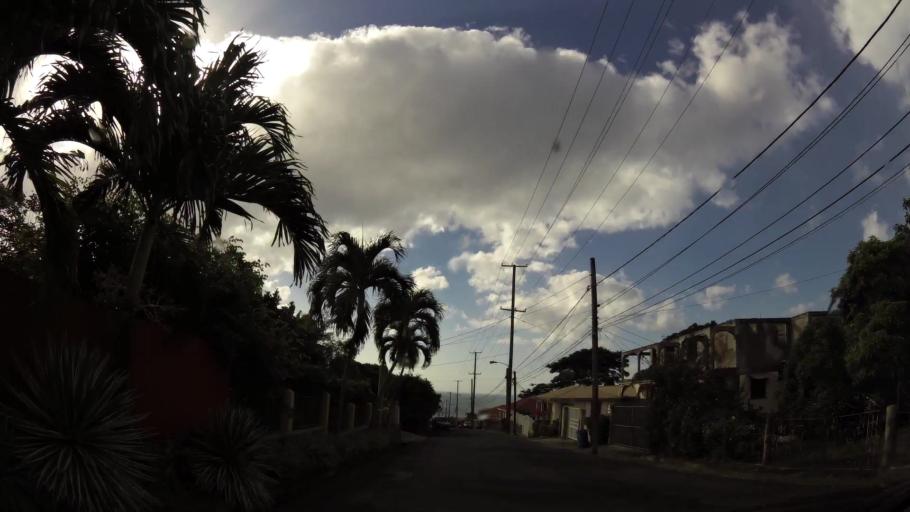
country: DM
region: Saint George
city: Roseau
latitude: 15.3054
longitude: -61.3785
